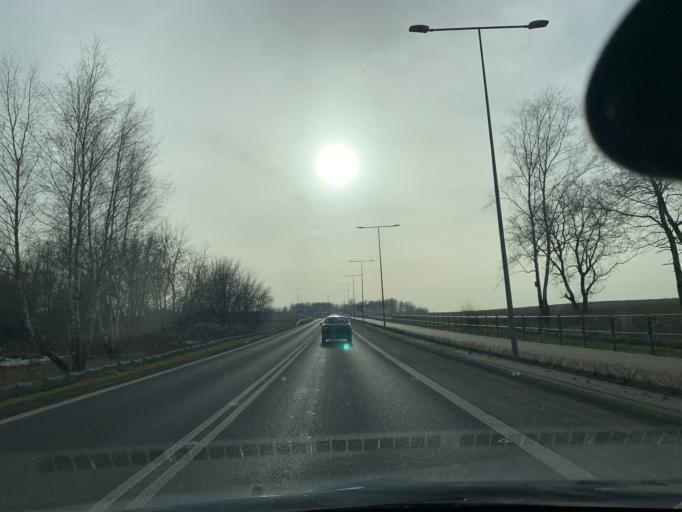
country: PL
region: Silesian Voivodeship
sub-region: Powiat tarnogorski
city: Radzionkow
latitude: 50.4077
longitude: 18.8958
